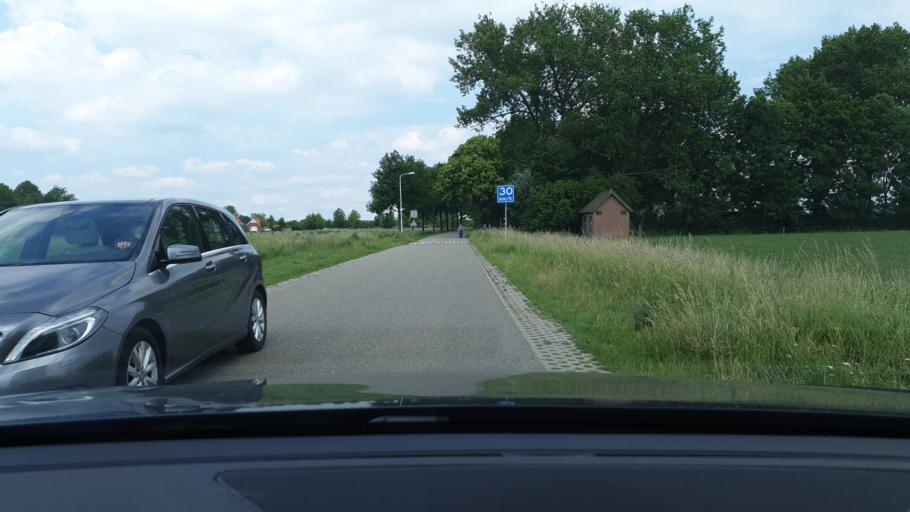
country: NL
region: Gelderland
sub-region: Gemeente Overbetuwe
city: Elst
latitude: 51.9065
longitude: 5.8913
